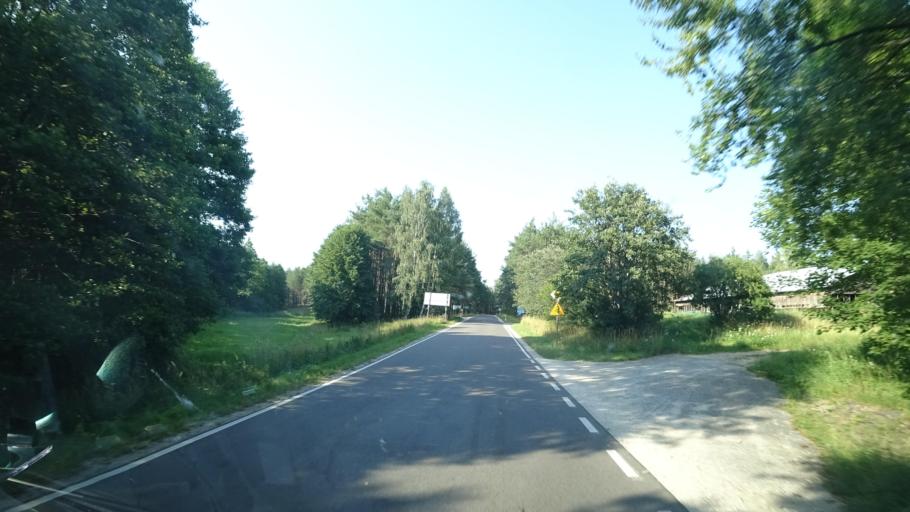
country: PL
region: Pomeranian Voivodeship
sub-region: Powiat bytowski
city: Lipnica
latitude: 53.8322
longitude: 17.4493
